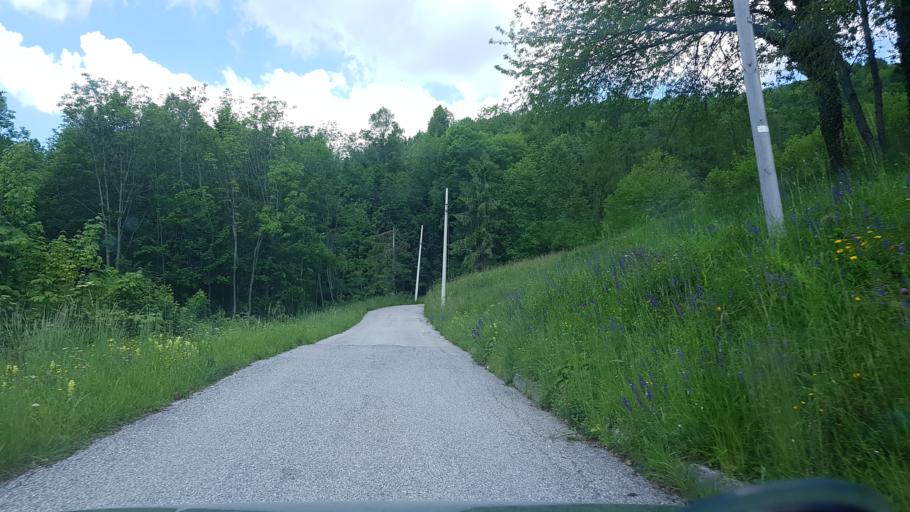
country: IT
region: Friuli Venezia Giulia
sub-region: Provincia di Udine
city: Torreano
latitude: 46.1763
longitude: 13.4309
